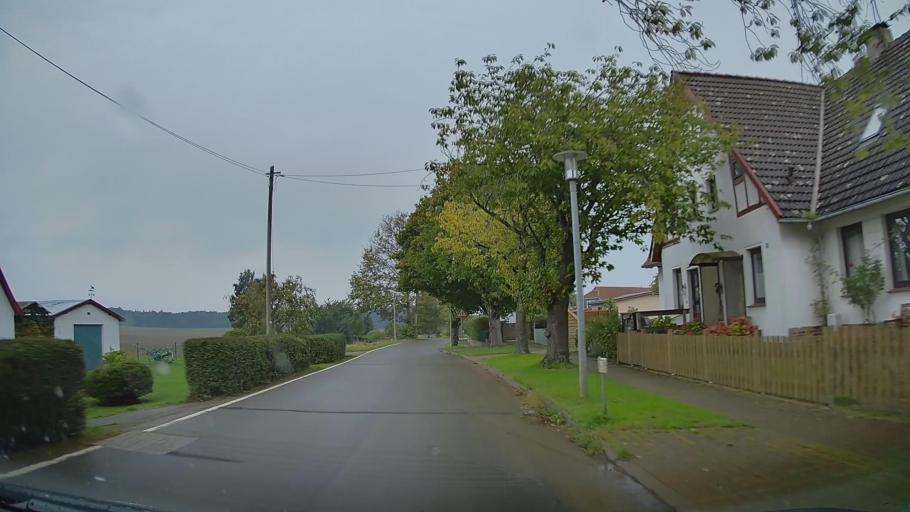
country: DE
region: Mecklenburg-Vorpommern
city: Kalkhorst
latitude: 53.9962
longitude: 11.0435
